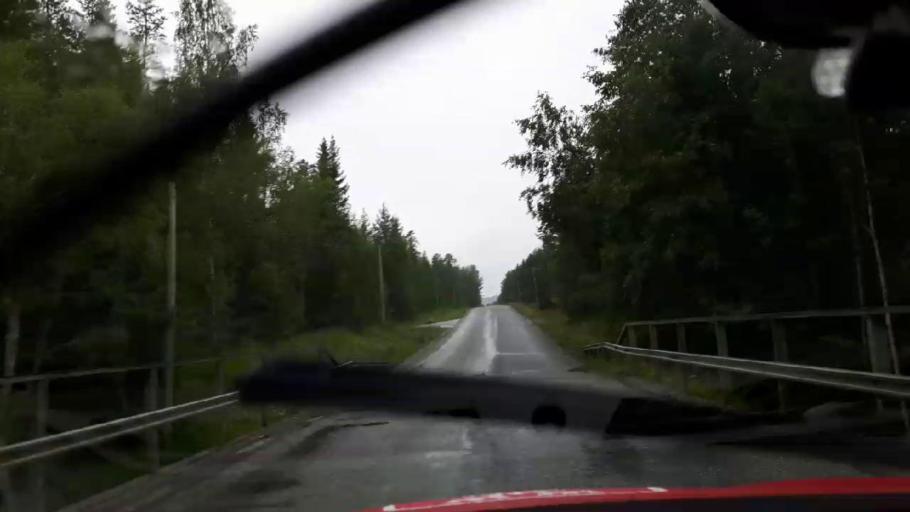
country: SE
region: Jaemtland
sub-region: OEstersunds Kommun
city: Brunflo
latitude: 62.7735
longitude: 15.0118
